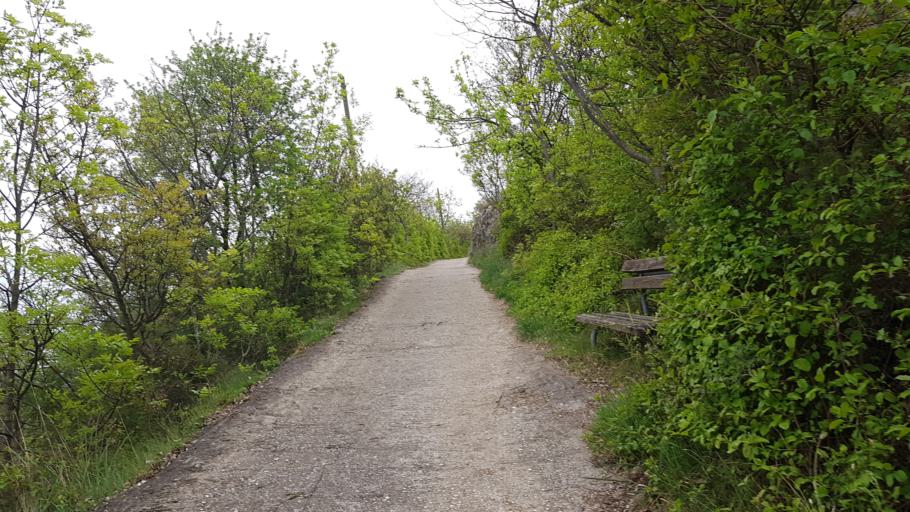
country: IT
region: Veneto
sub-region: Provincia di Verona
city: Parona
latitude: 45.4702
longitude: 10.9713
